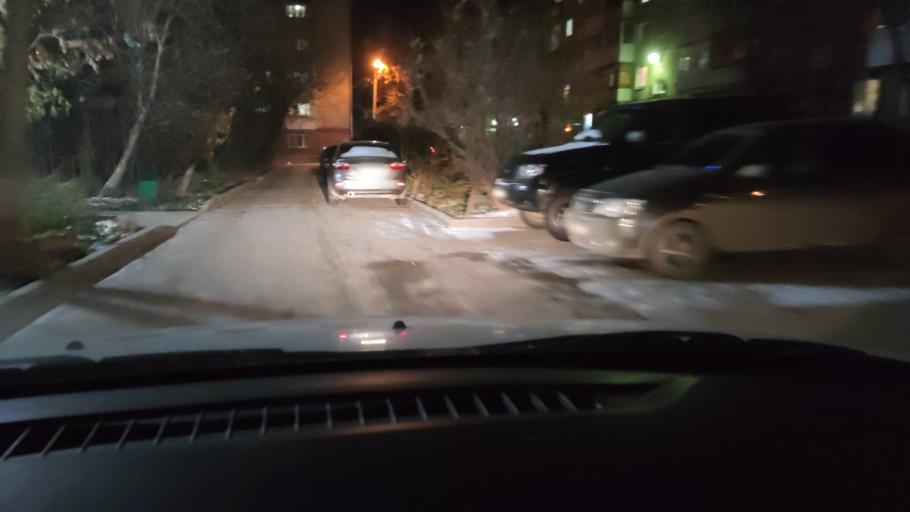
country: RU
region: Perm
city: Perm
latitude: 57.9780
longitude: 56.2780
